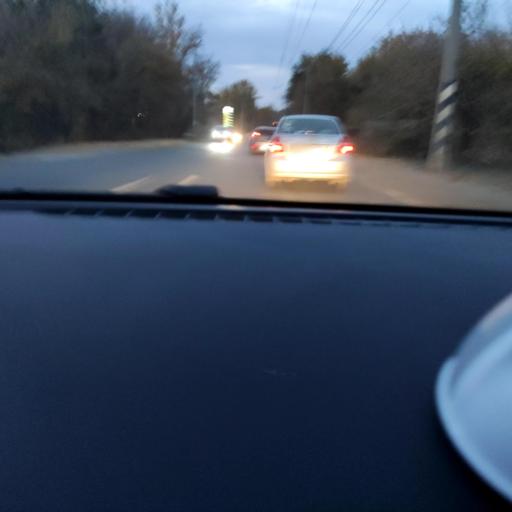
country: RU
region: Samara
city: Samara
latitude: 53.1474
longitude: 50.0953
